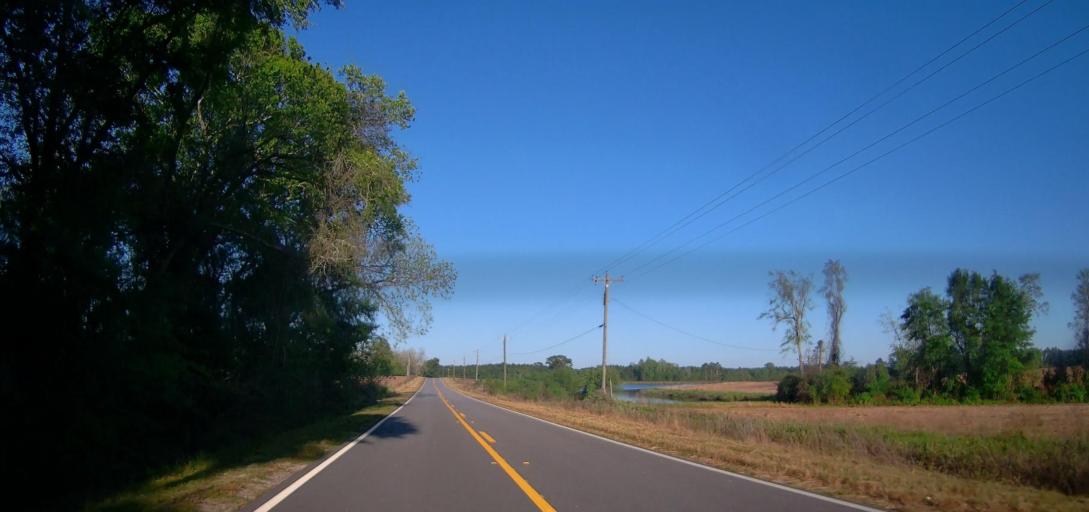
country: US
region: Georgia
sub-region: Ben Hill County
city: Fitzgerald
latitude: 31.6563
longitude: -83.1685
